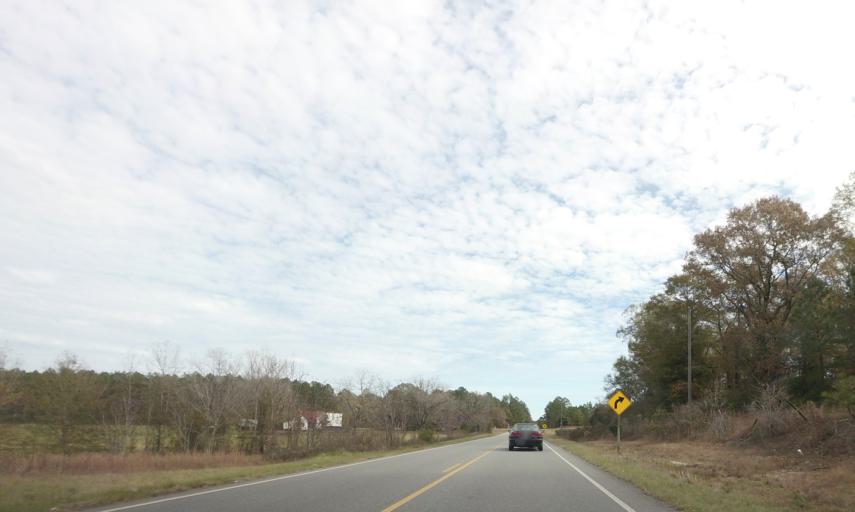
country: US
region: Georgia
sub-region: Dodge County
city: Chester
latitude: 32.4101
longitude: -83.2488
